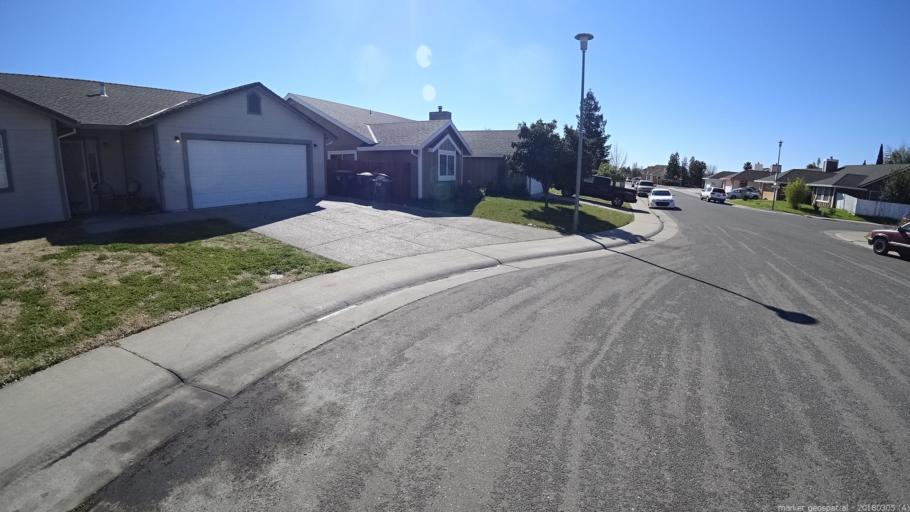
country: US
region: California
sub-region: Sacramento County
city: Florin
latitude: 38.4885
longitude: -121.4184
